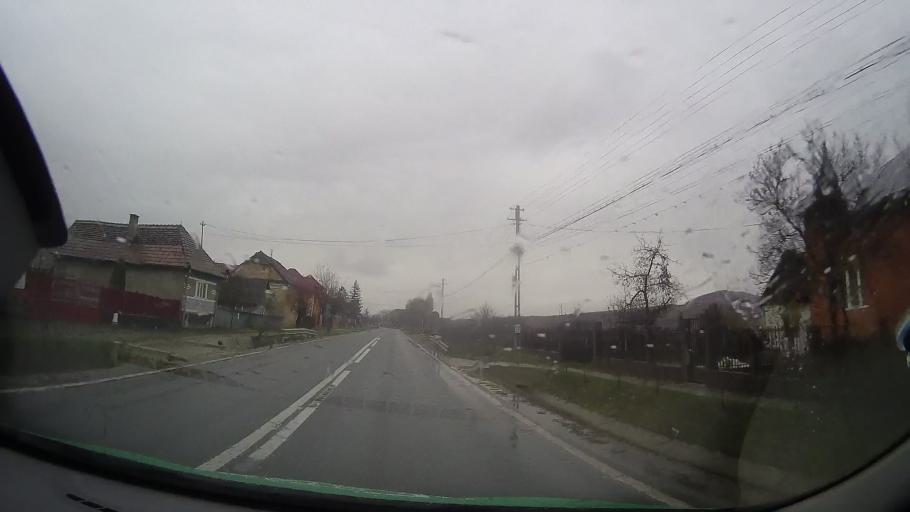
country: RO
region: Bistrita-Nasaud
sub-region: Comuna Galatii Bistritei
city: Galatii Bistritei
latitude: 46.9739
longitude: 24.4330
